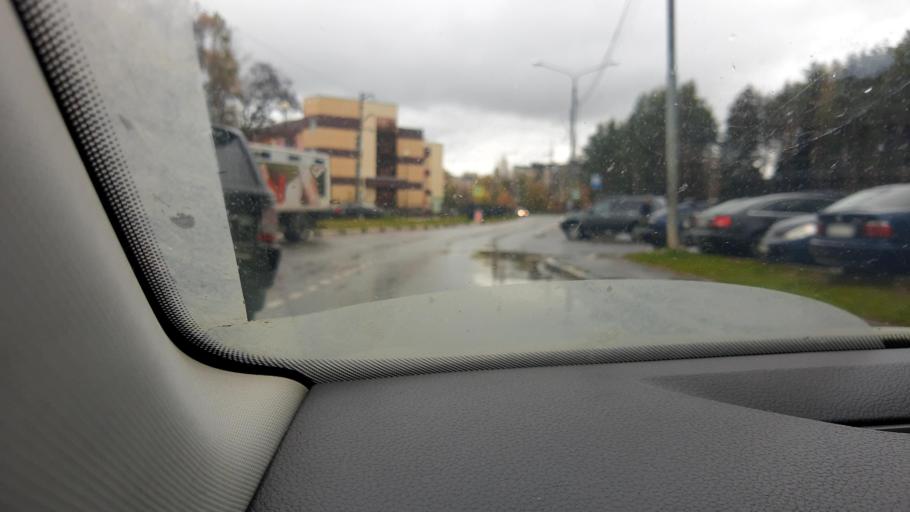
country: RU
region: Moskovskaya
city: Aprelevka
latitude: 55.5473
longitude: 37.0844
